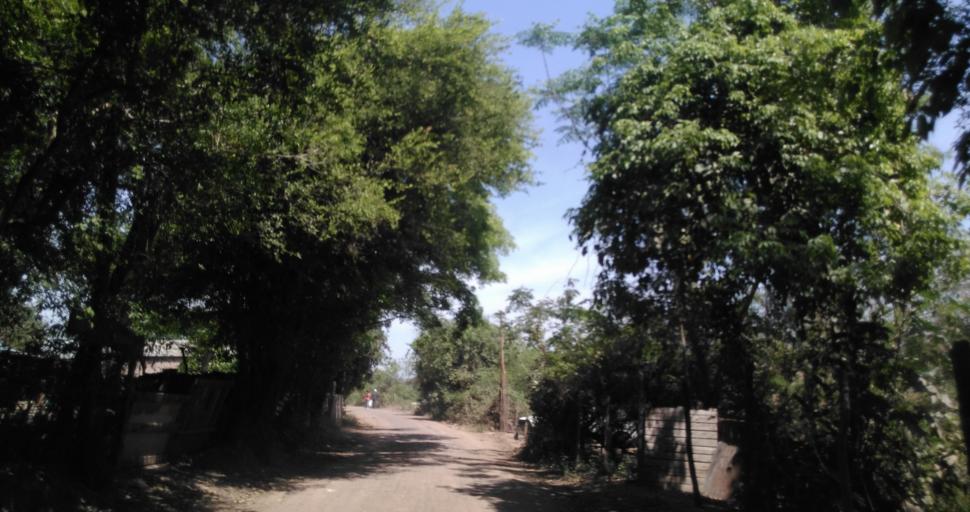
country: AR
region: Chaco
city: Fontana
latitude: -27.4186
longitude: -59.0109
